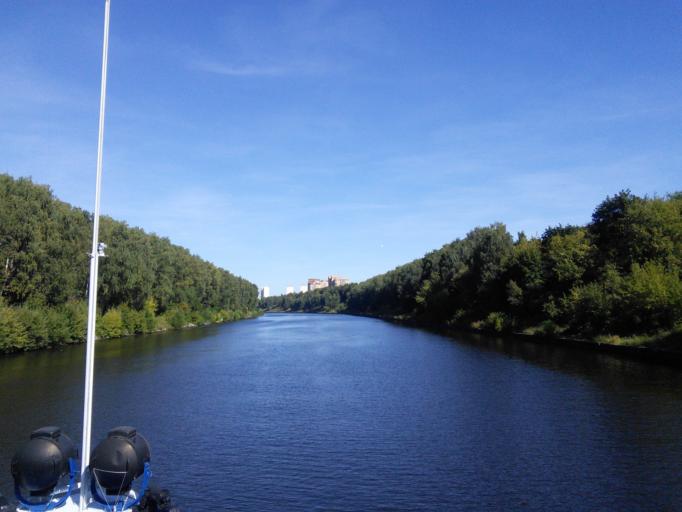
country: RU
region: Moskovskaya
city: Dolgoprudnyy
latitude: 55.9249
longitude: 37.4887
